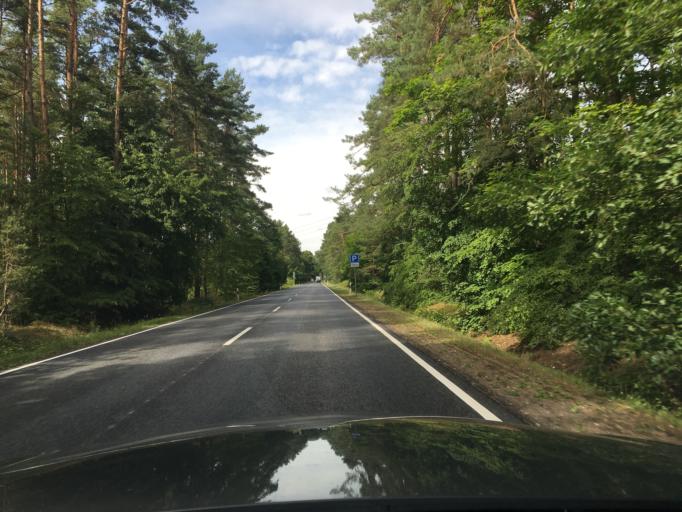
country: DE
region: Brandenburg
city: Furstenberg
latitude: 53.2147
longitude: 13.1270
